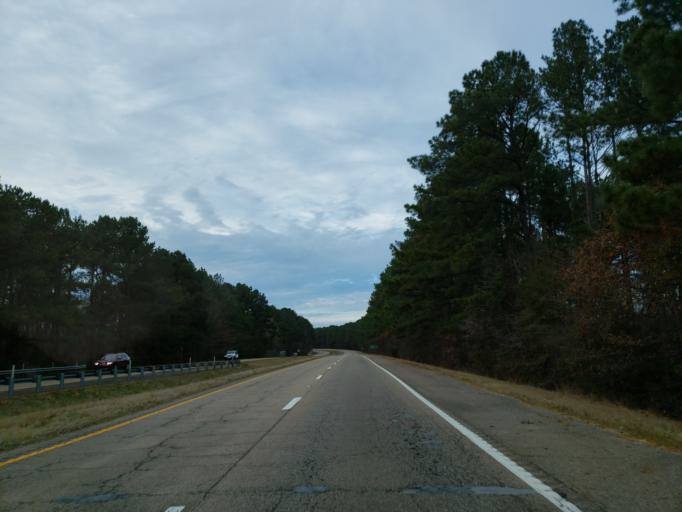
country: US
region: Mississippi
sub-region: Lauderdale County
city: Marion
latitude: 32.3946
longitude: -88.6389
